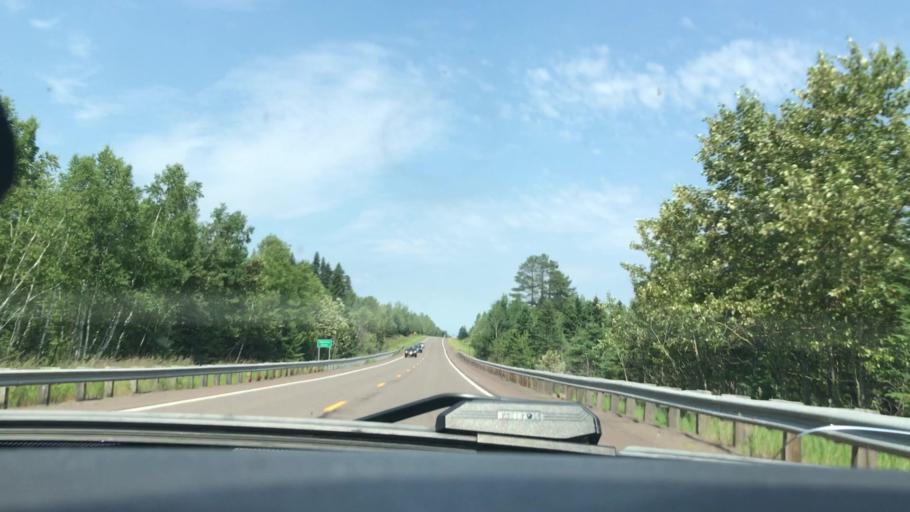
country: US
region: Minnesota
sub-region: Lake County
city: Silver Bay
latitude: 47.4435
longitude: -91.0697
